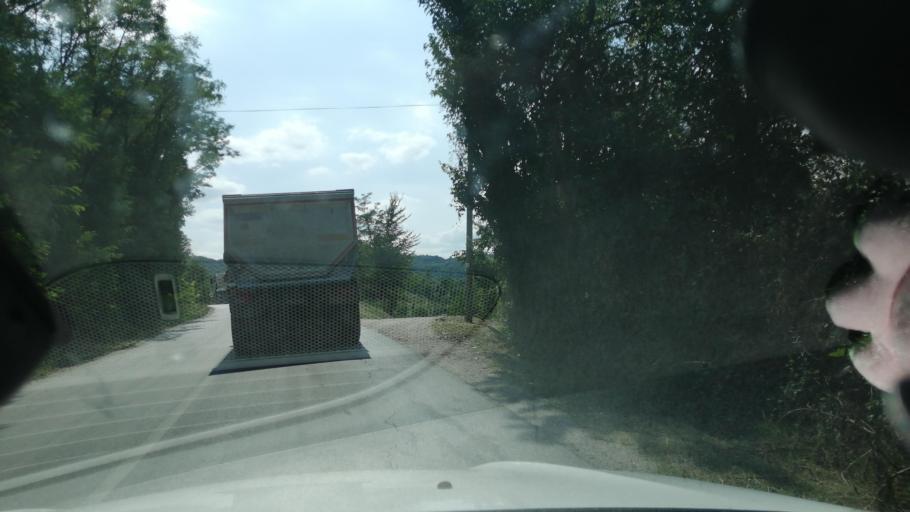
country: RS
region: Central Serbia
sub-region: Moravicki Okrug
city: Cacak
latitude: 43.8589
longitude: 20.3090
